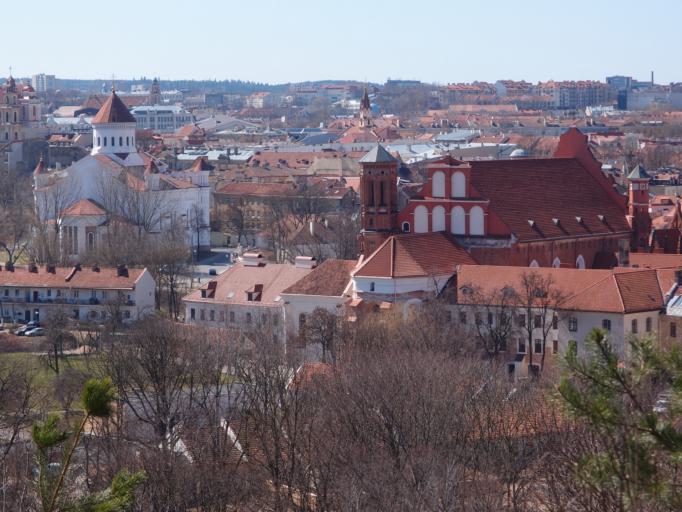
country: LT
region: Vilnius County
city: Rasos
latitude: 54.6864
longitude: 25.2978
